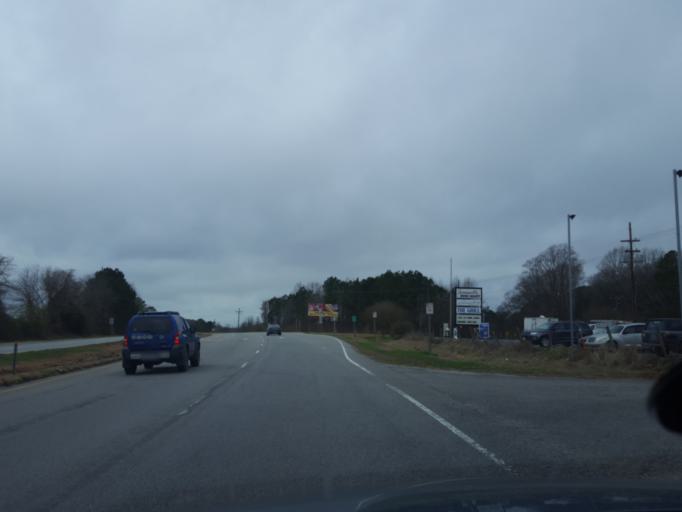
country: US
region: North Carolina
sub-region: Washington County
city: Plymouth
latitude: 35.8084
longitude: -76.8861
